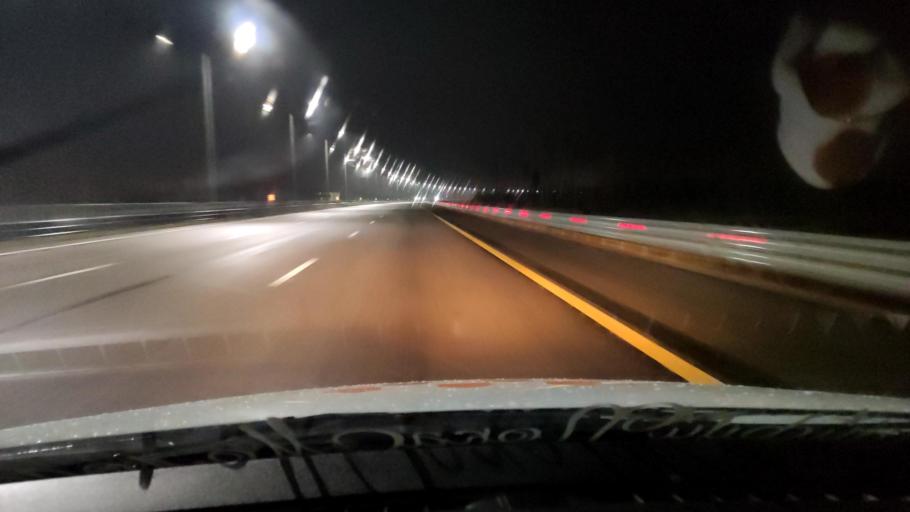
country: RU
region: Voronezj
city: Somovo
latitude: 51.7674
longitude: 39.3049
